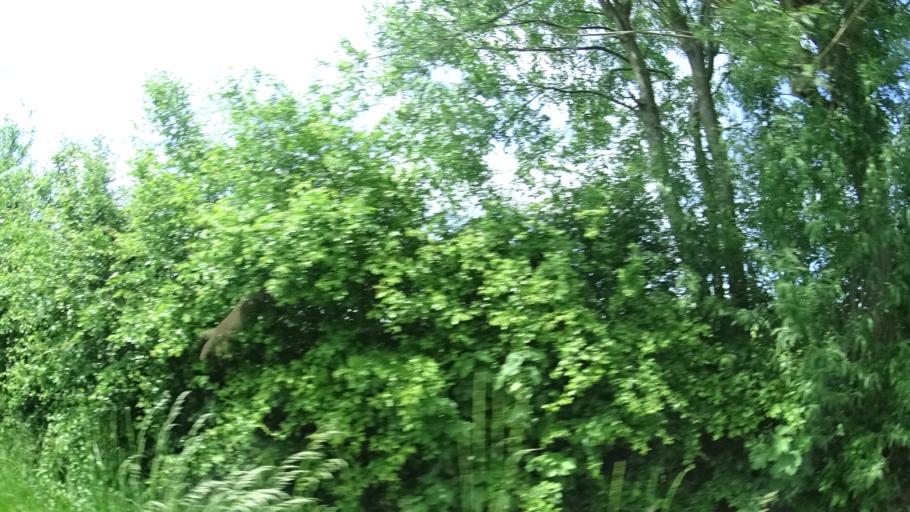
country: DE
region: Thuringia
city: Stadtilm
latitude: 50.7531
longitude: 11.1181
